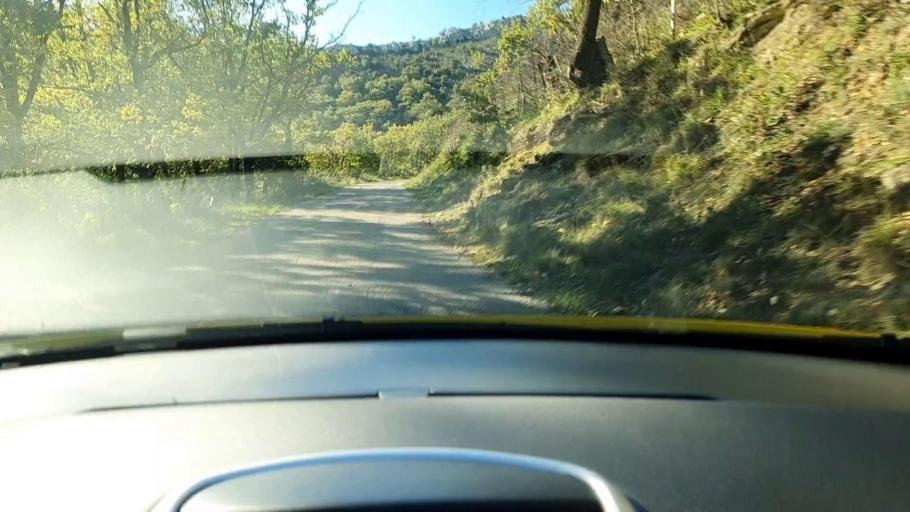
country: FR
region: Languedoc-Roussillon
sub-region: Departement du Gard
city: Sumene
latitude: 43.9777
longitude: 3.7546
